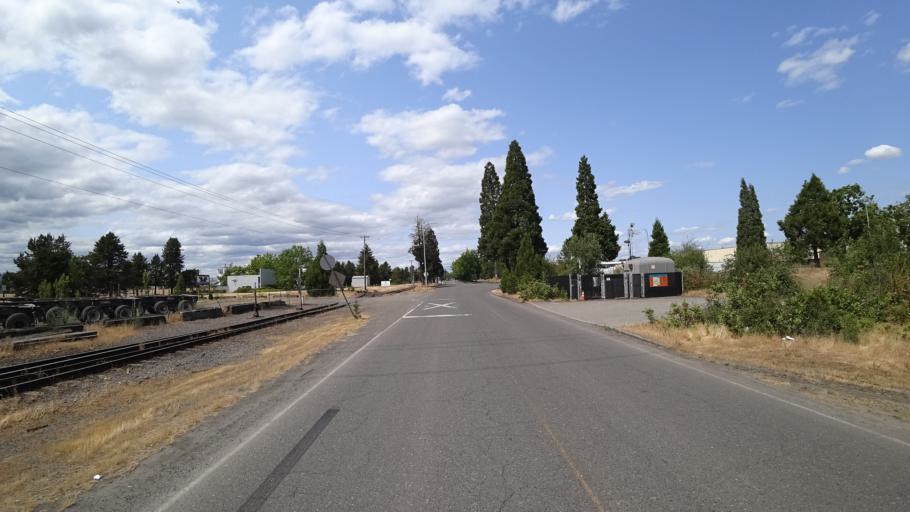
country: US
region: Oregon
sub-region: Washington County
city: Oak Hills
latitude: 45.6186
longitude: -122.7803
